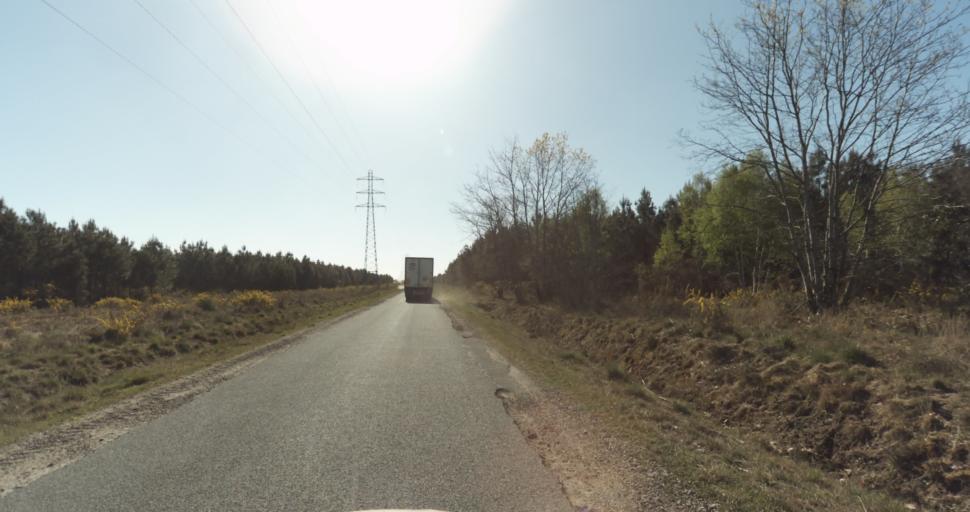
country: FR
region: Aquitaine
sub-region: Departement de la Gironde
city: Marcheprime
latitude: 44.7500
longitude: -0.8461
